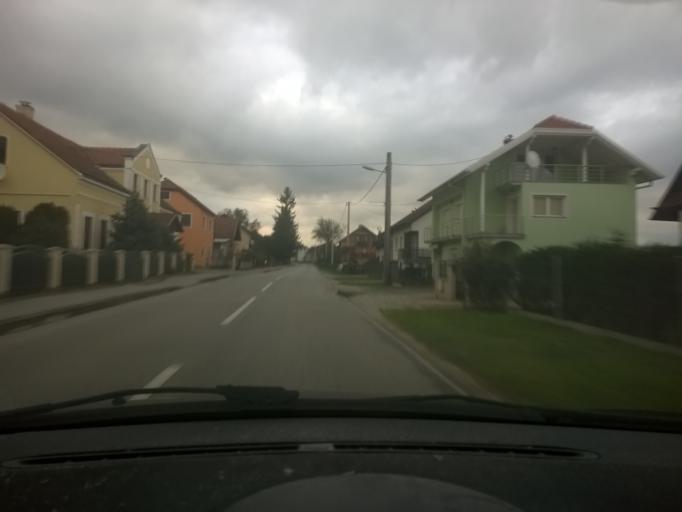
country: HR
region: Zagrebacka
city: Jakovlje
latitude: 45.9924
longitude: 15.8444
